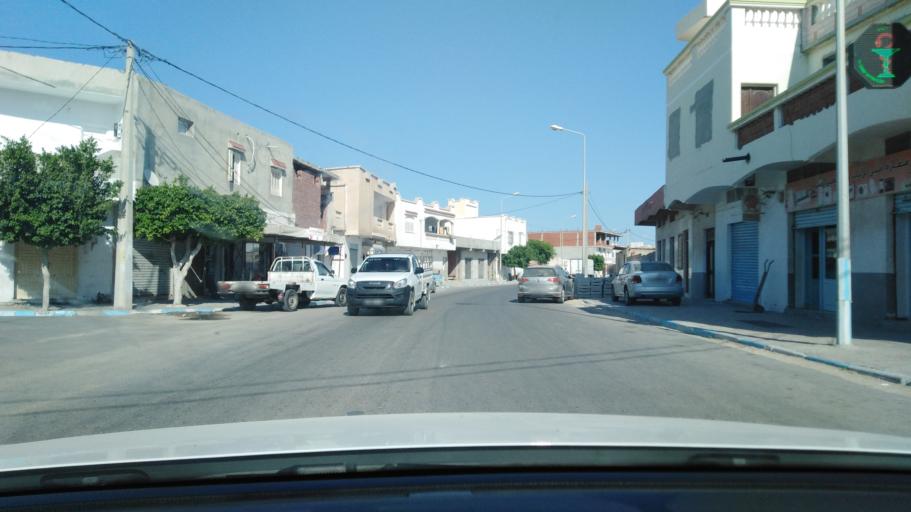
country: TN
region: Qabis
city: Gabes
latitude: 33.9381
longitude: 10.0657
